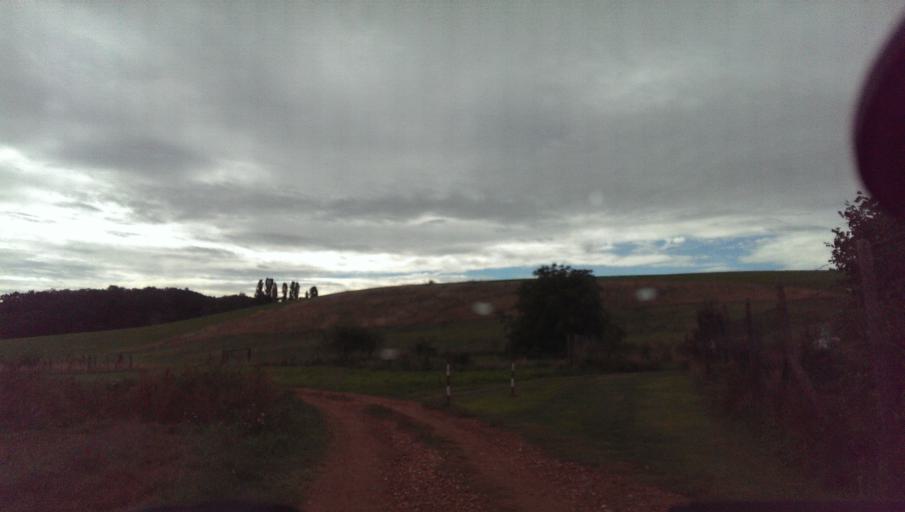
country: CZ
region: South Moravian
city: Moravsky Pisek
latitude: 48.9960
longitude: 17.3137
